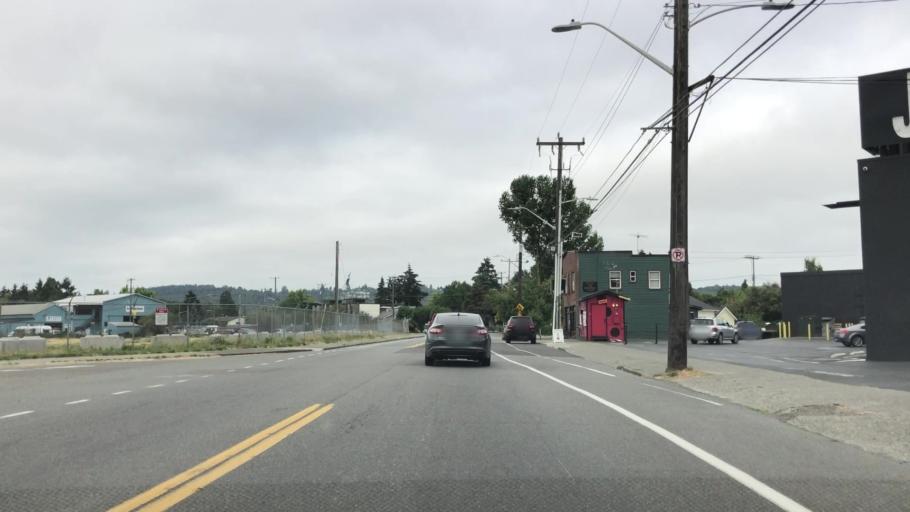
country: US
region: Washington
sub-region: King County
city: White Center
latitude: 47.5488
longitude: -122.3168
